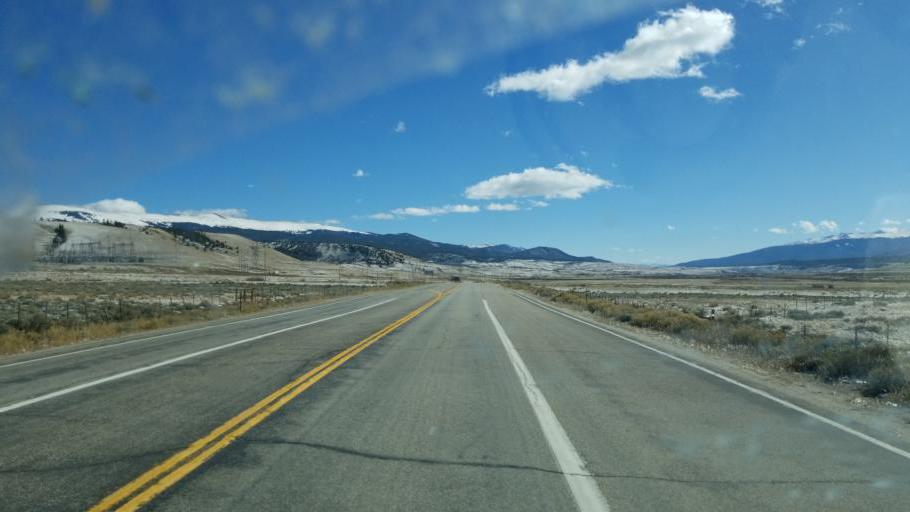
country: US
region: Colorado
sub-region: Lake County
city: Leadville
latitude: 39.1918
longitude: -106.3336
